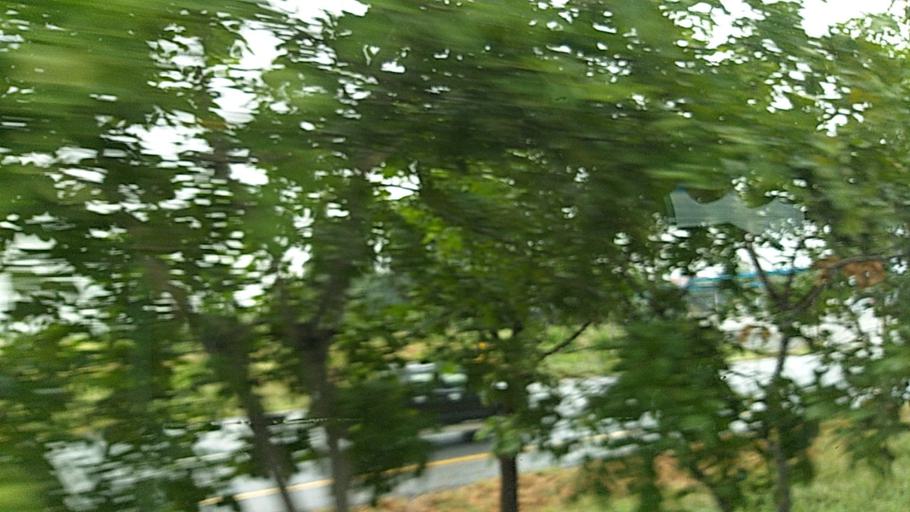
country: TH
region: Nakhon Ratchasima
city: Non Sung
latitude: 15.2218
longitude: 102.3623
